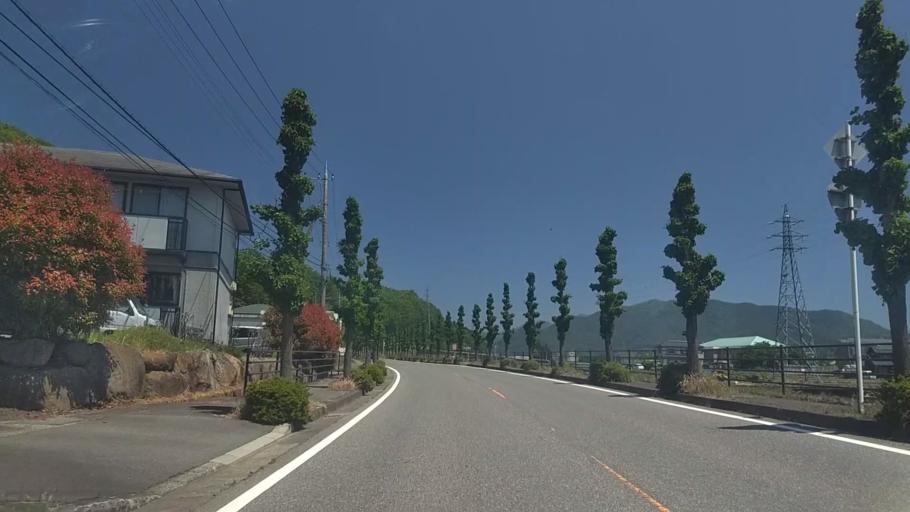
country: JP
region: Yamanashi
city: Nirasaki
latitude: 35.7975
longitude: 138.4244
